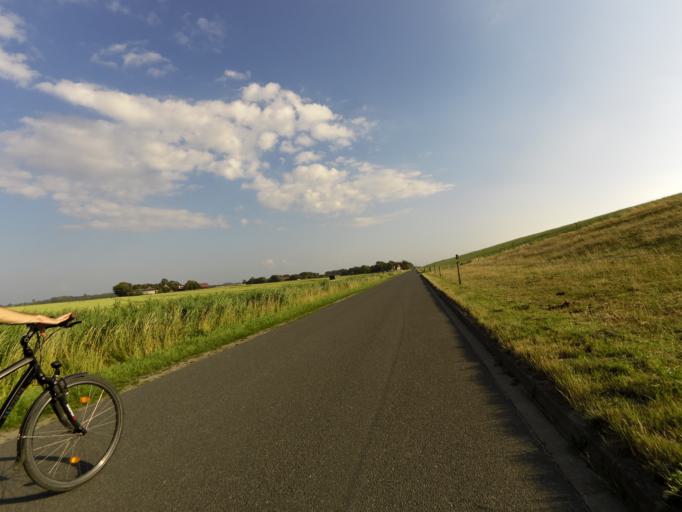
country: DE
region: Lower Saxony
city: Nordholz
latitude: 53.7814
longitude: 8.5498
